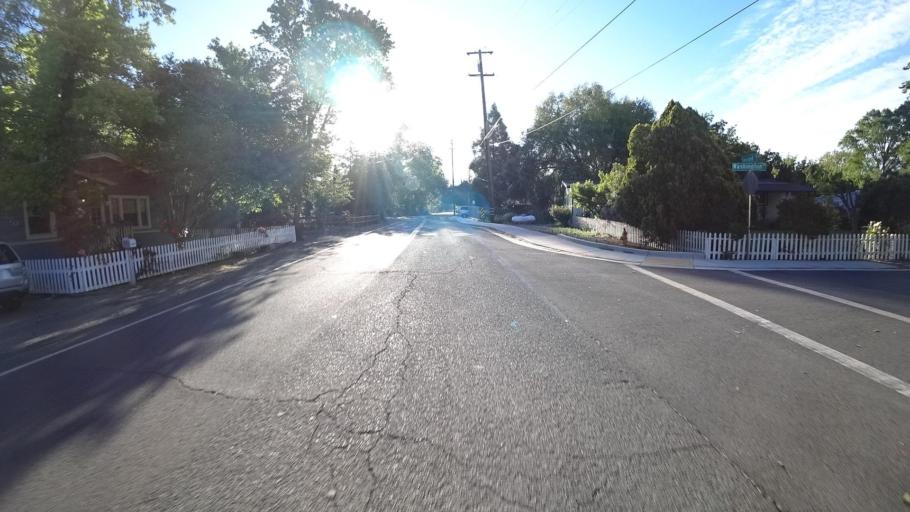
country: US
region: California
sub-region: Lake County
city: Upper Lake
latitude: 39.1657
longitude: -122.9097
